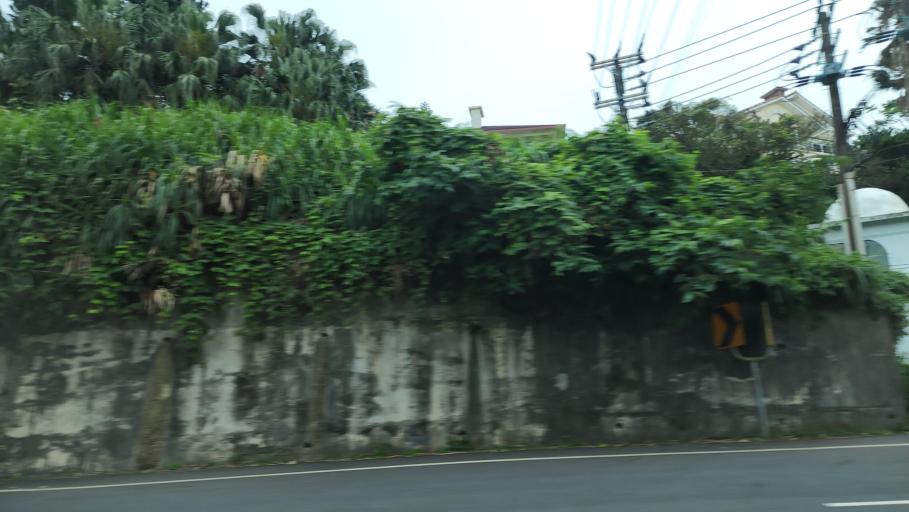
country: TW
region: Taiwan
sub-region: Keelung
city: Keelung
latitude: 25.1904
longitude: 121.6797
